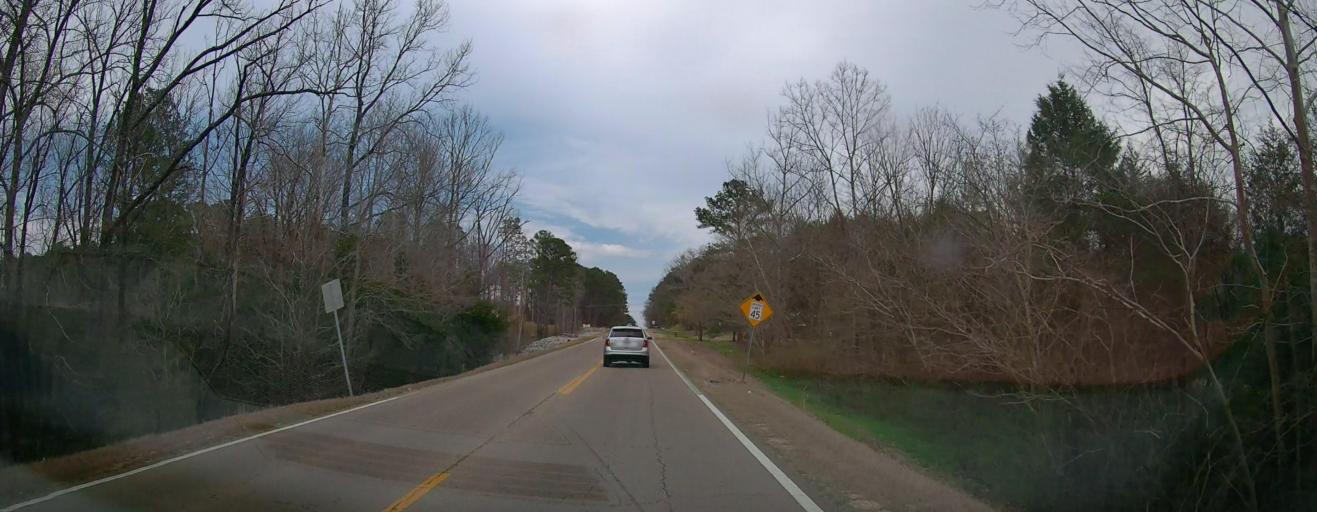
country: US
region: Mississippi
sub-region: Lee County
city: Plantersville
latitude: 34.2664
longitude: -88.5923
